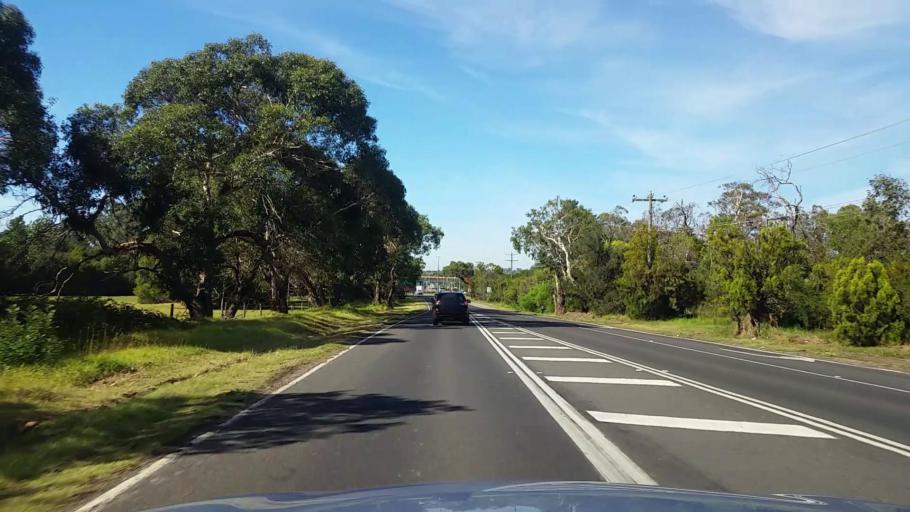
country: AU
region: Victoria
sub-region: Mornington Peninsula
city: Baxter
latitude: -38.1917
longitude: 145.1468
